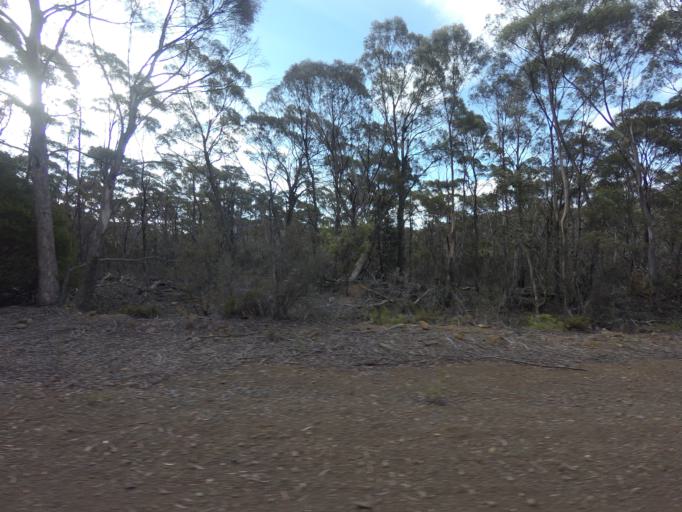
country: AU
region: Tasmania
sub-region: Break O'Day
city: St Helens
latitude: -41.8566
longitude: 148.0254
